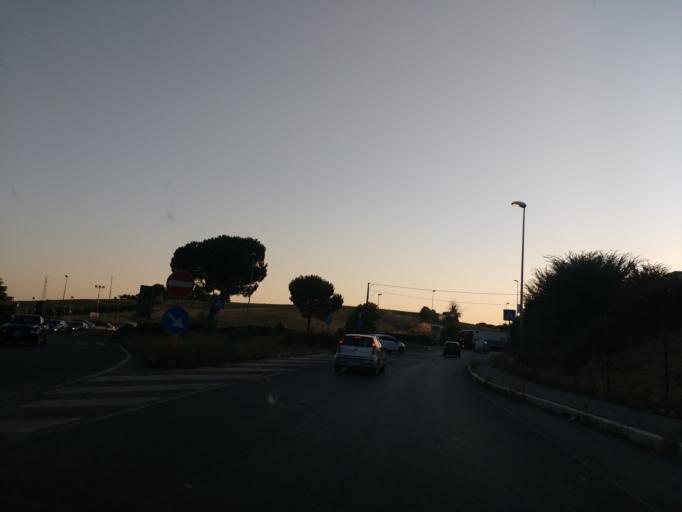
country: IT
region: Latium
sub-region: Citta metropolitana di Roma Capitale
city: Setteville
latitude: 41.9427
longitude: 12.6566
